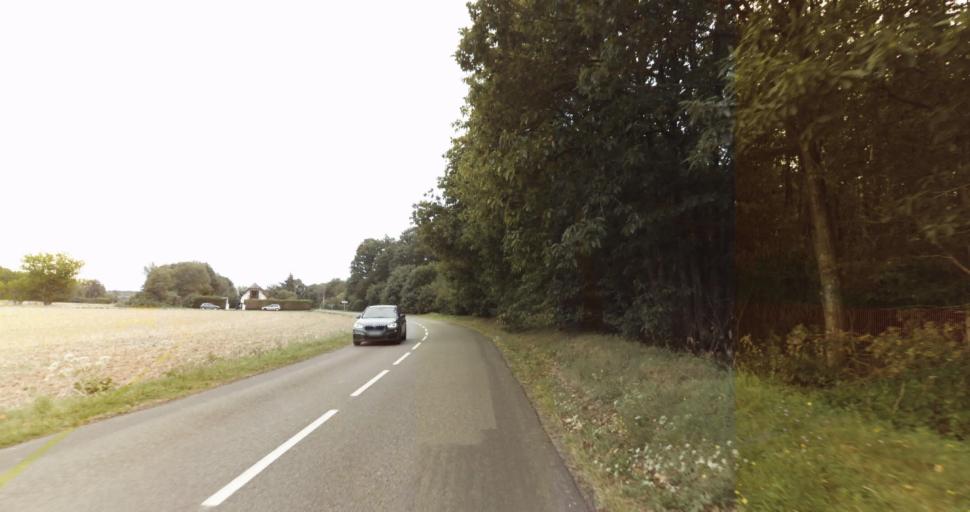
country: FR
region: Haute-Normandie
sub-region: Departement de l'Eure
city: Menilles
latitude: 48.9786
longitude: 1.2784
